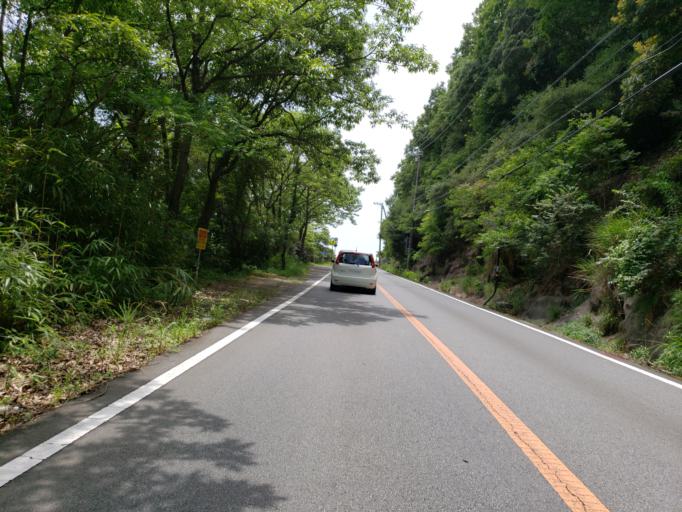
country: JP
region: Hyogo
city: Aioi
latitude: 34.7742
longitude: 134.4992
